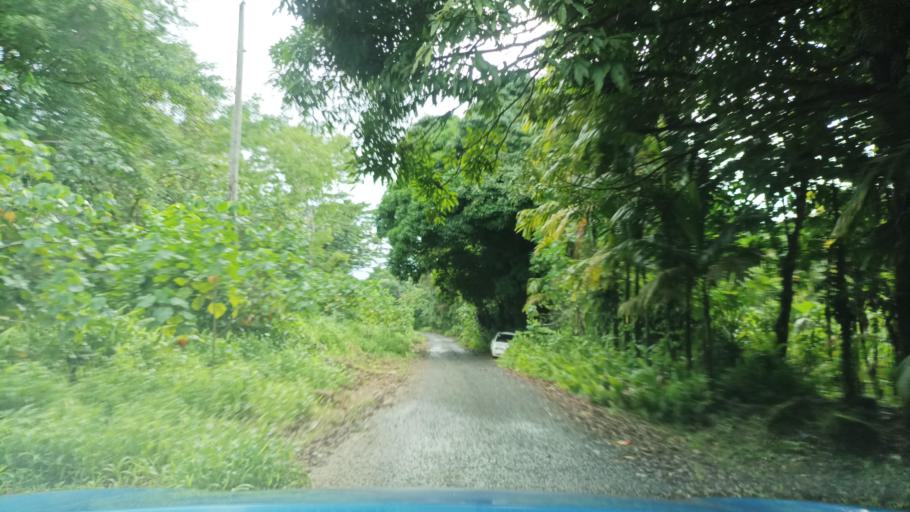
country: FM
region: Pohnpei
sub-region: Sokehs Municipality
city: Palikir - National Government Center
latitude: 6.8803
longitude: 158.1670
